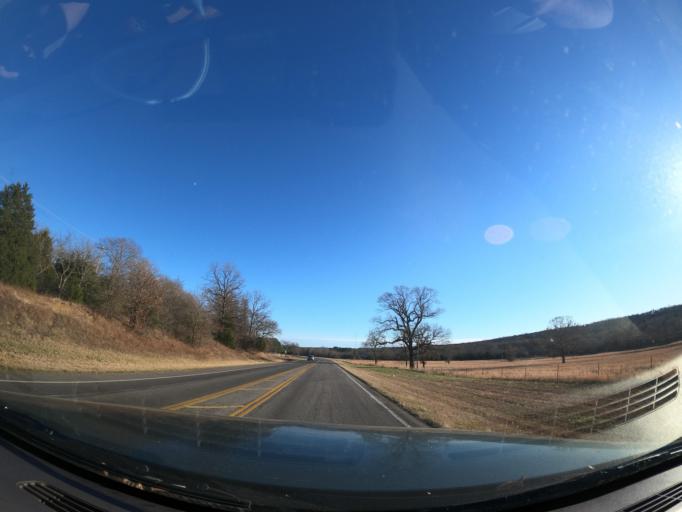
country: US
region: Oklahoma
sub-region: Latimer County
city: Wilburton
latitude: 34.9297
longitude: -95.3373
